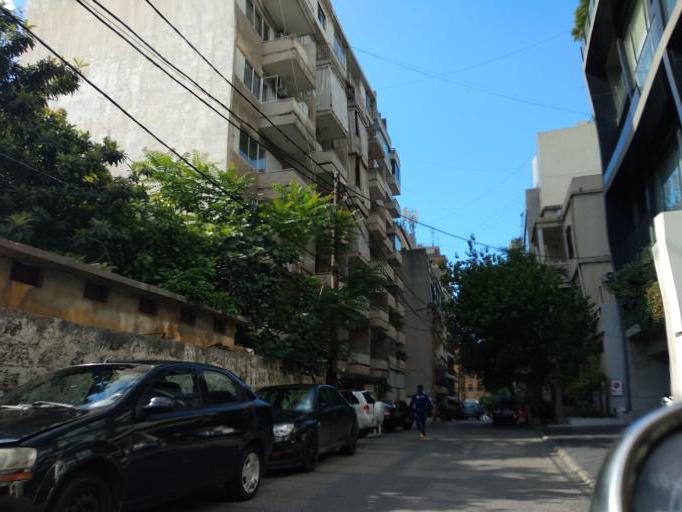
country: LB
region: Beyrouth
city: Beirut
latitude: 33.8868
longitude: 35.5233
